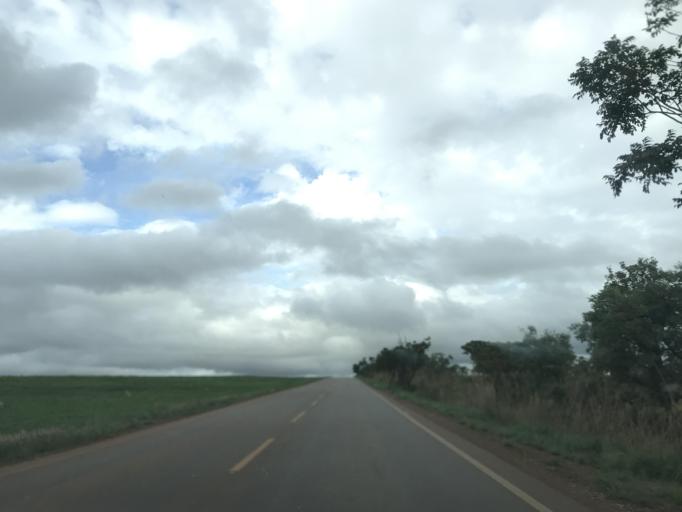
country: BR
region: Goias
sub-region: Vianopolis
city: Vianopolis
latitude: -16.5605
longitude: -48.2832
